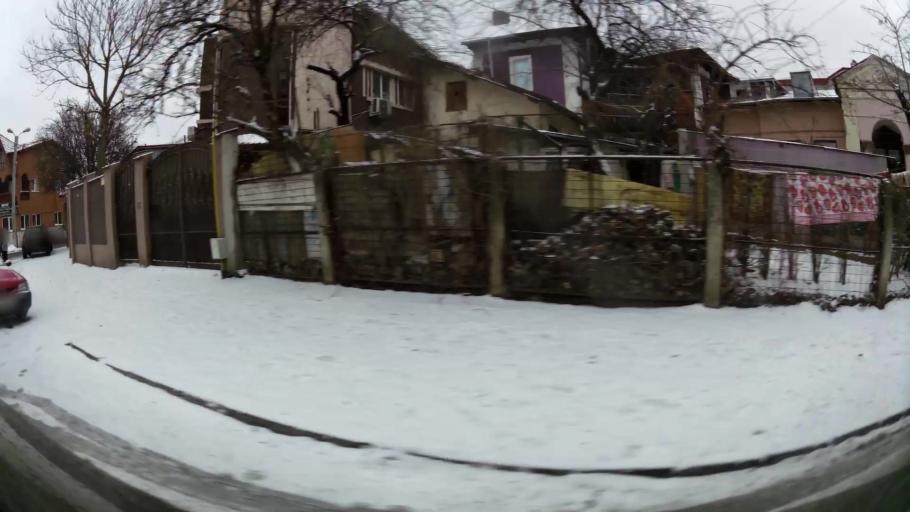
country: RO
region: Prahova
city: Ploiesti
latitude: 44.9380
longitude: 26.0324
